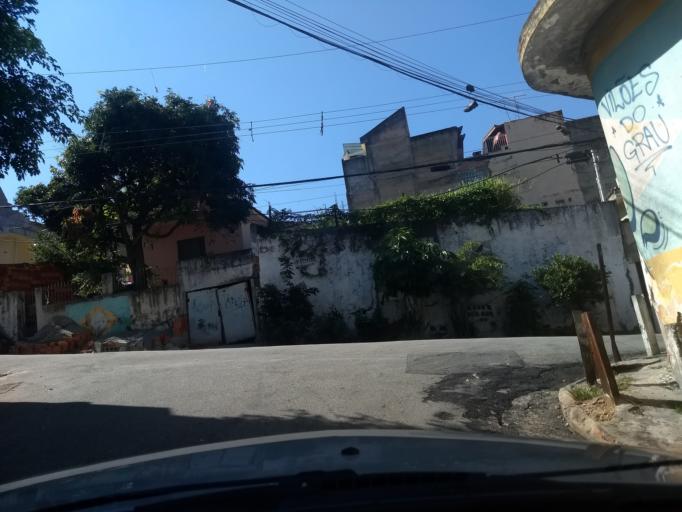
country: BR
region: Sao Paulo
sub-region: Sao Paulo
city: Sao Paulo
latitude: -23.4957
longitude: -46.5946
